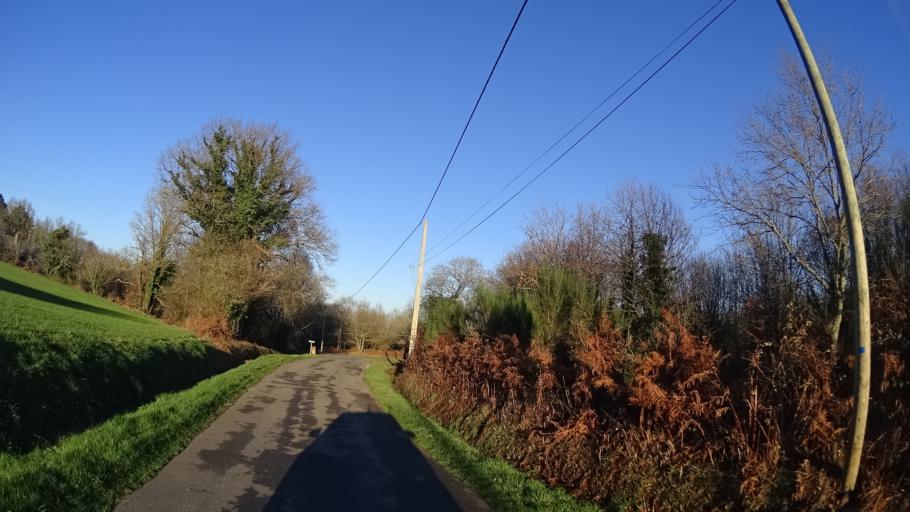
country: FR
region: Brittany
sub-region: Departement du Morbihan
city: Saint-Jean-la-Poterie
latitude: 47.6531
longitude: -2.1366
